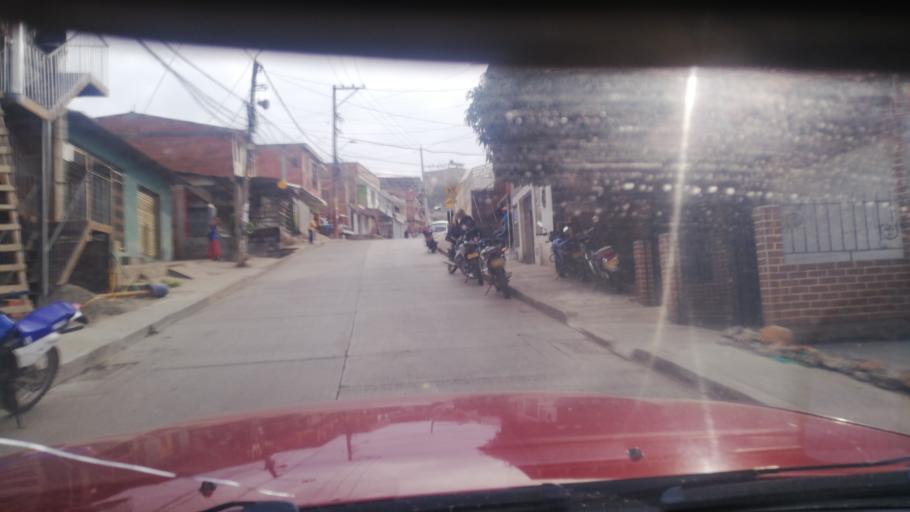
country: CO
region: Valle del Cauca
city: Cali
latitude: 3.4843
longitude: -76.5519
